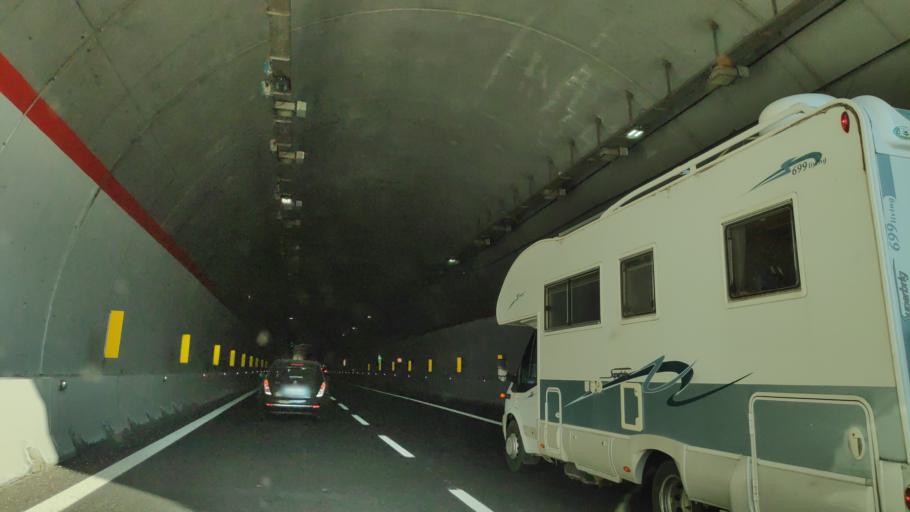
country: IT
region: Basilicate
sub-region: Provincia di Potenza
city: Lagonegro
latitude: 40.1614
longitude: 15.7344
